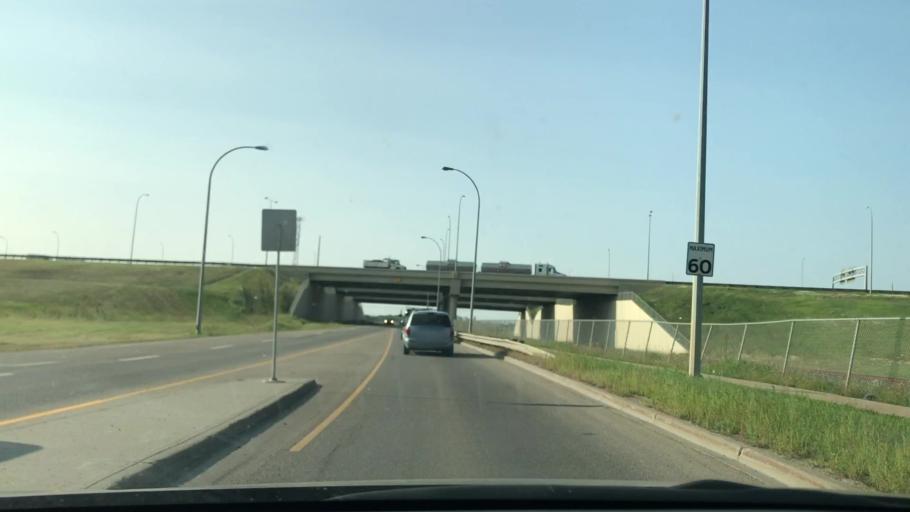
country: CA
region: Alberta
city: Beaumont
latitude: 53.4393
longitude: -113.4843
